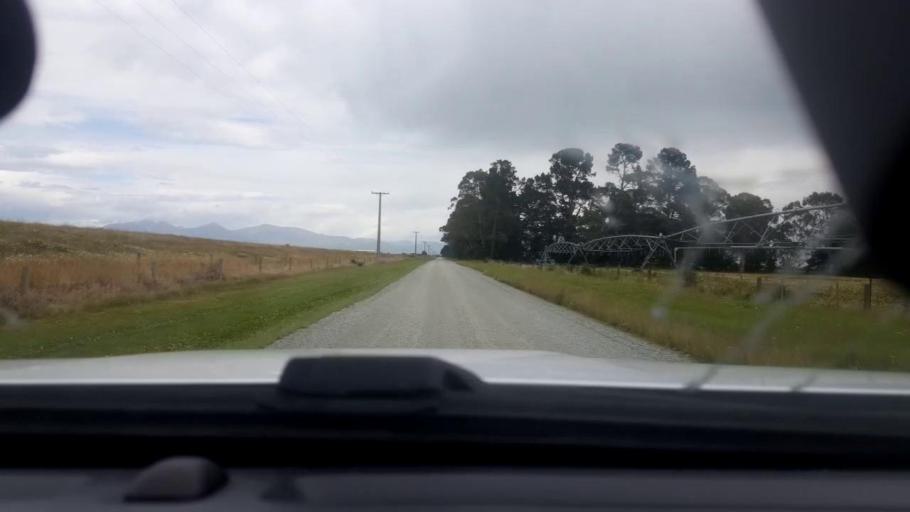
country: NZ
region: Canterbury
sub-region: Timaru District
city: Pleasant Point
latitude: -44.1523
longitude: 171.3958
